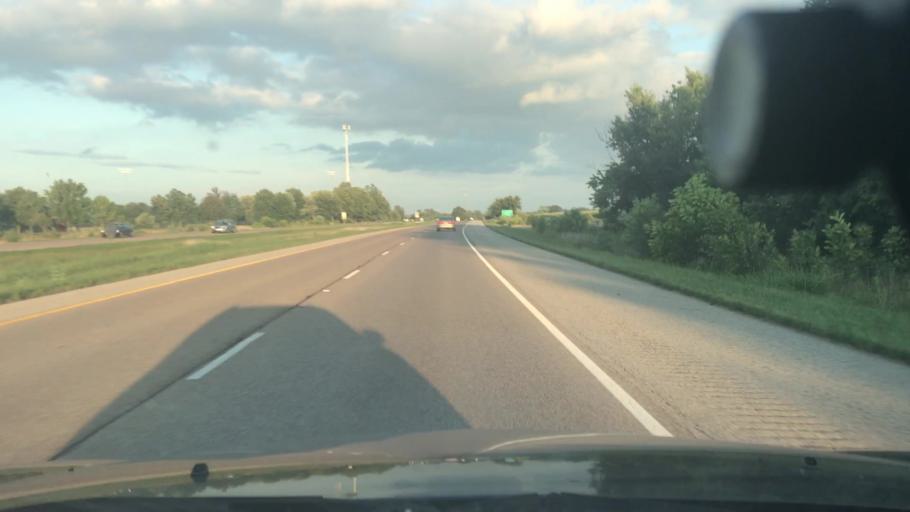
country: US
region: Illinois
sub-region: Clinton County
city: Albers
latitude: 38.5064
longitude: -89.6266
